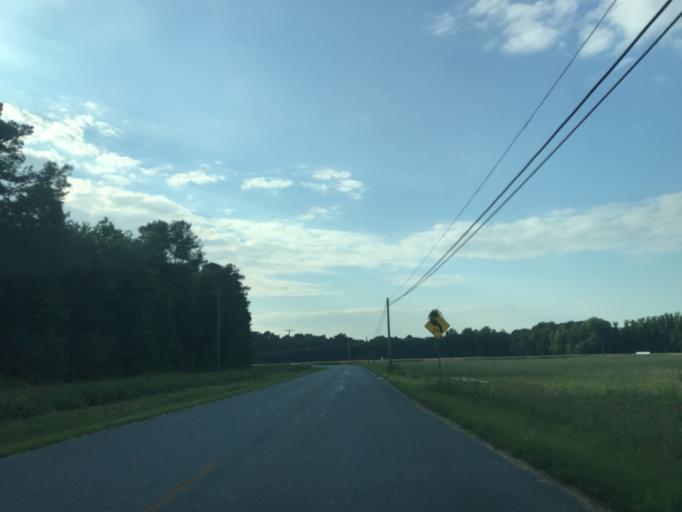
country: US
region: Maryland
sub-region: Caroline County
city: Federalsburg
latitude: 38.7199
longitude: -75.7812
